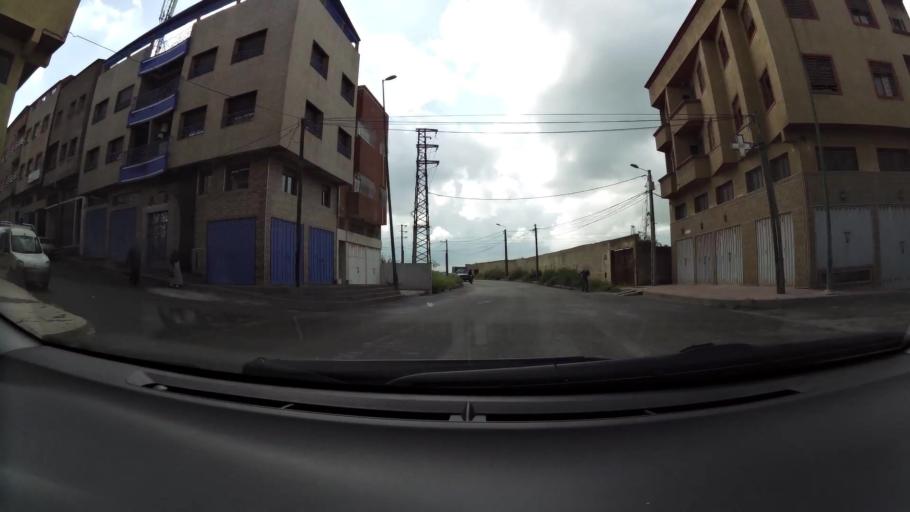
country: MA
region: Grand Casablanca
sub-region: Mediouna
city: Tit Mellil
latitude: 33.5441
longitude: -7.4881
